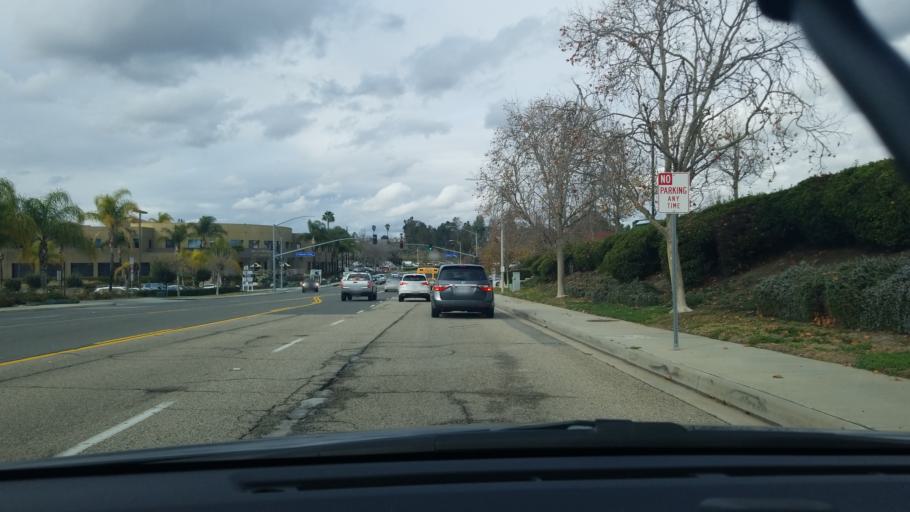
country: US
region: California
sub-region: Riverside County
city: Murrieta Hot Springs
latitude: 33.5568
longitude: -117.1844
